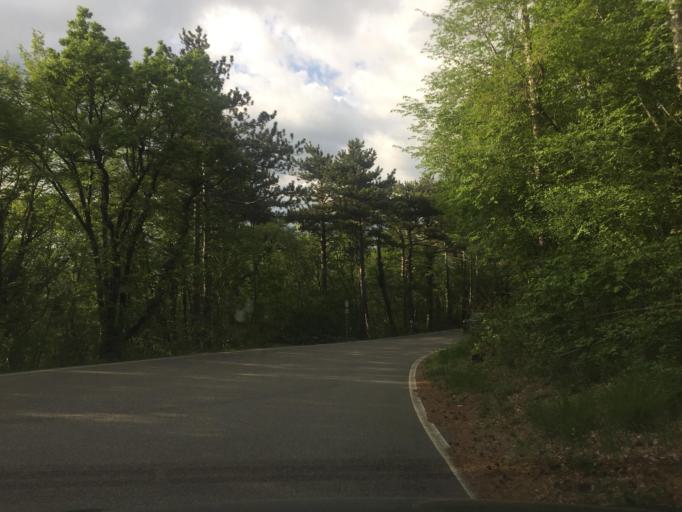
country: IT
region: Friuli Venezia Giulia
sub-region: Provincia di Trieste
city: Dolina
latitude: 45.6359
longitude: 13.8715
